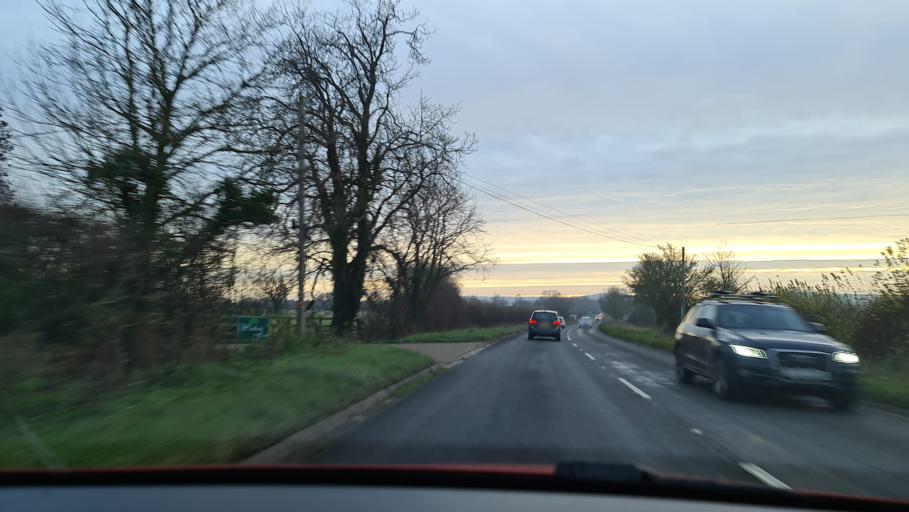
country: GB
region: England
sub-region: Buckinghamshire
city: Haddenham
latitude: 51.7534
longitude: -0.8964
